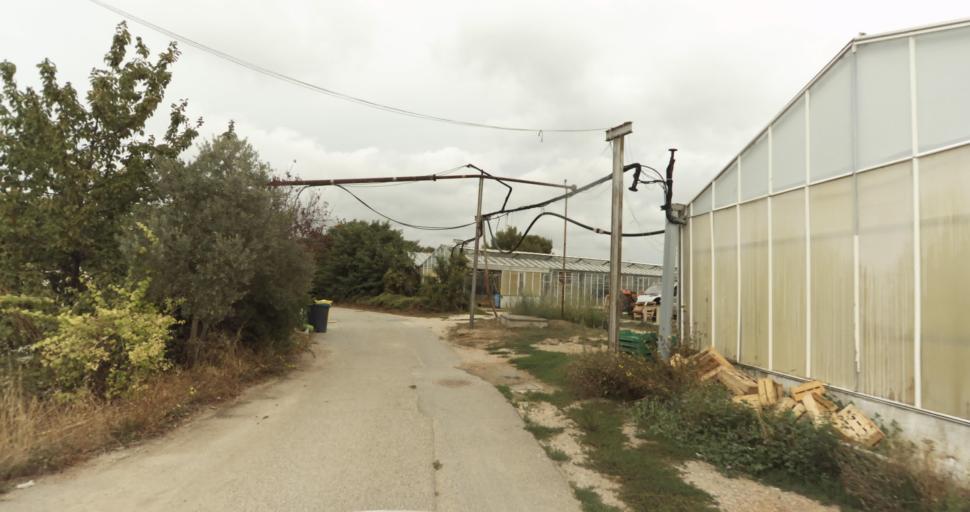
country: FR
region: Provence-Alpes-Cote d'Azur
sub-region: Departement des Bouches-du-Rhone
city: Saint-Victoret
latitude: 43.4136
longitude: 5.2729
